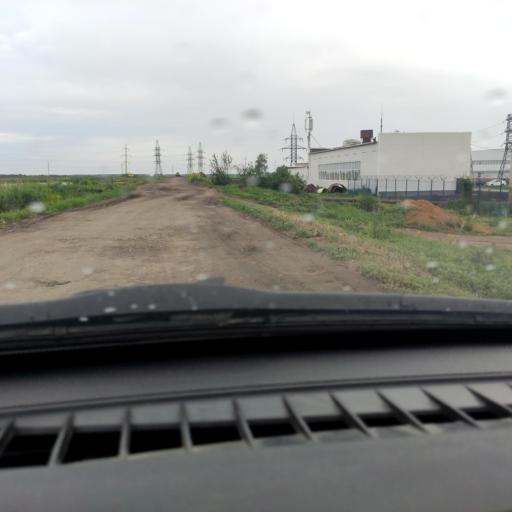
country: RU
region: Samara
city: Tol'yatti
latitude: 53.5915
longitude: 49.4393
